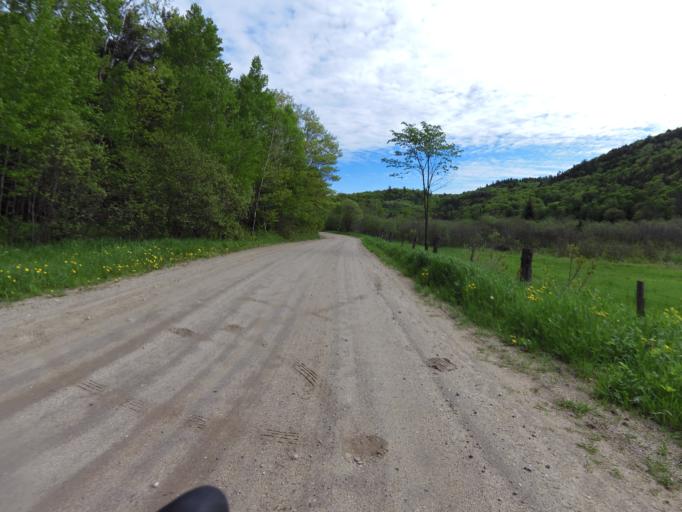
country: CA
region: Quebec
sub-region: Outaouais
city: Wakefield
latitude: 45.7807
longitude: -75.9160
